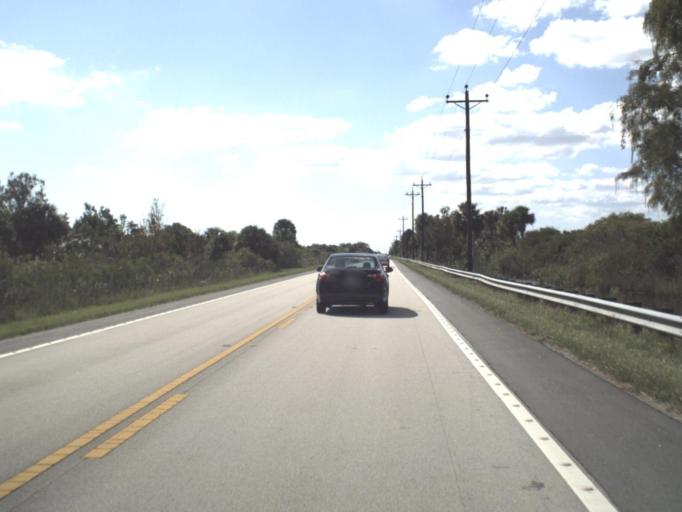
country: US
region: Florida
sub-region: Collier County
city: Marco
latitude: 25.9016
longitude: -81.2989
